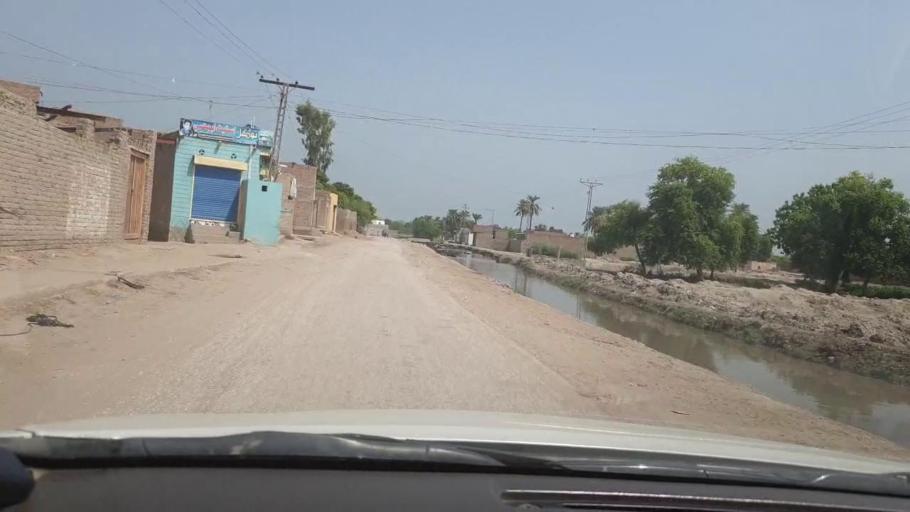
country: PK
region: Sindh
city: Shikarpur
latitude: 27.9437
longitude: 68.6354
